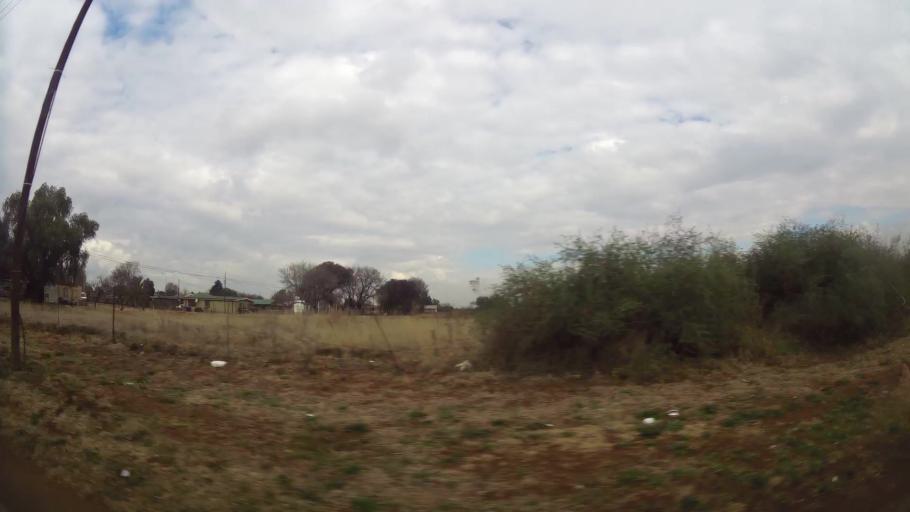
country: ZA
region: Gauteng
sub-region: Sedibeng District Municipality
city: Meyerton
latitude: -26.5927
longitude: 27.9941
